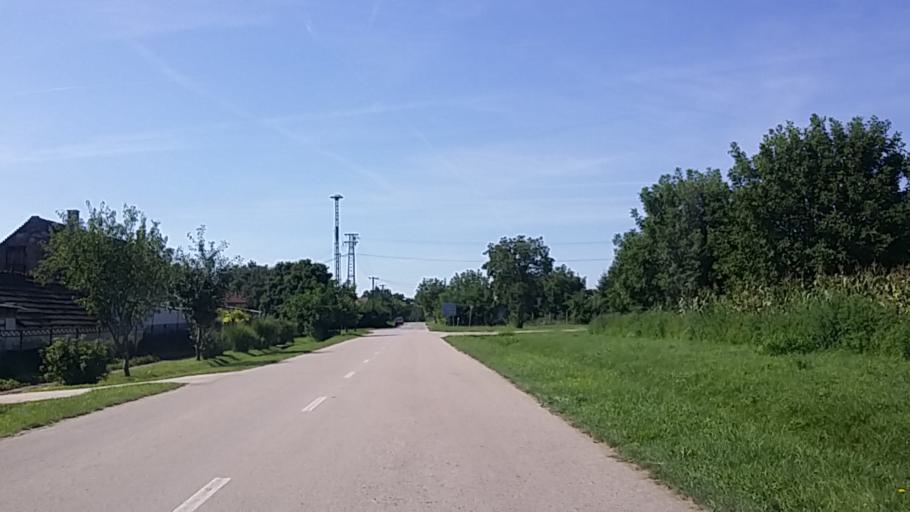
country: HU
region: Fejer
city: Deg
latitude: 46.8767
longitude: 18.4445
